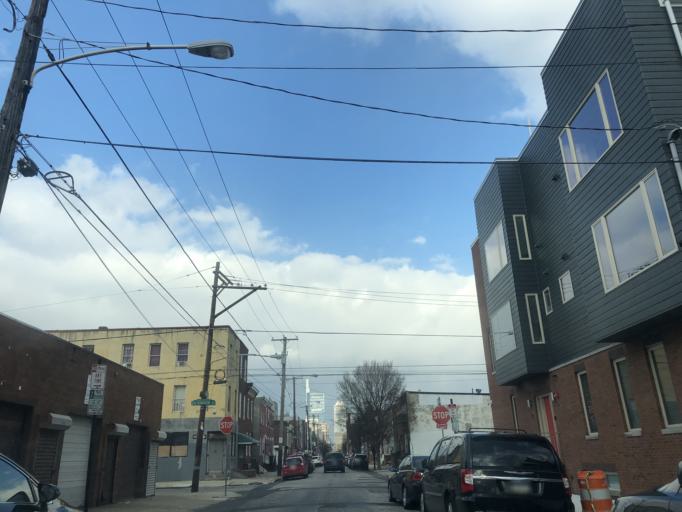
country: US
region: Pennsylvania
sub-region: Philadelphia County
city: Philadelphia
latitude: 39.9357
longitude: -75.1739
